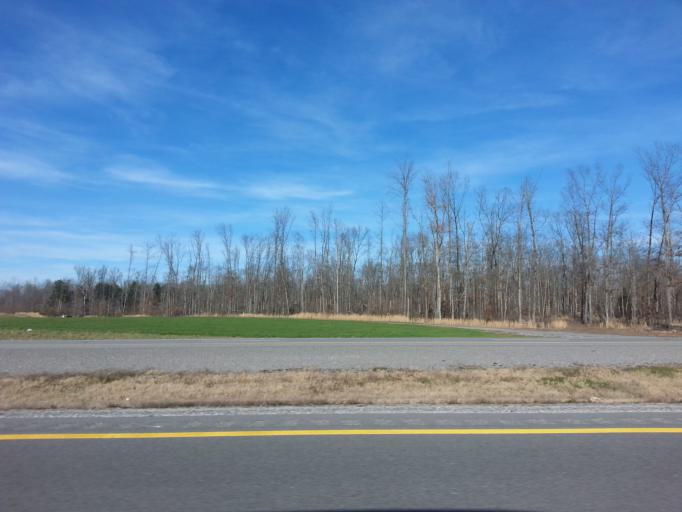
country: US
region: Tennessee
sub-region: Cannon County
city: Woodbury
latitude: 35.7362
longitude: -85.9351
